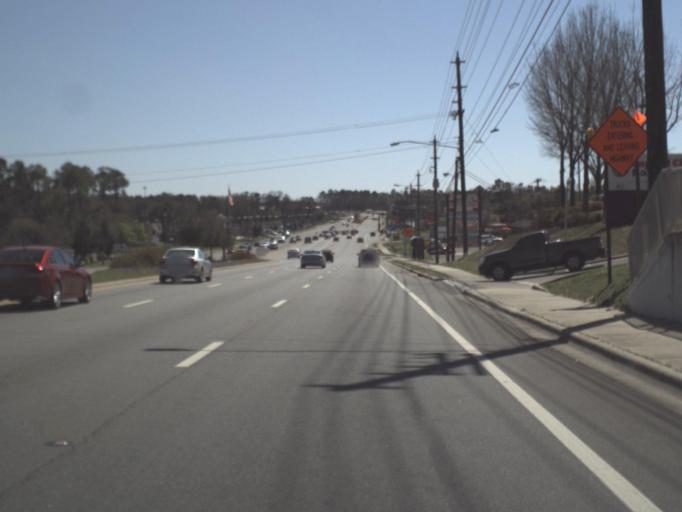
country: US
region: Florida
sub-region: Leon County
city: Tallahassee
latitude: 30.4629
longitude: -84.3613
